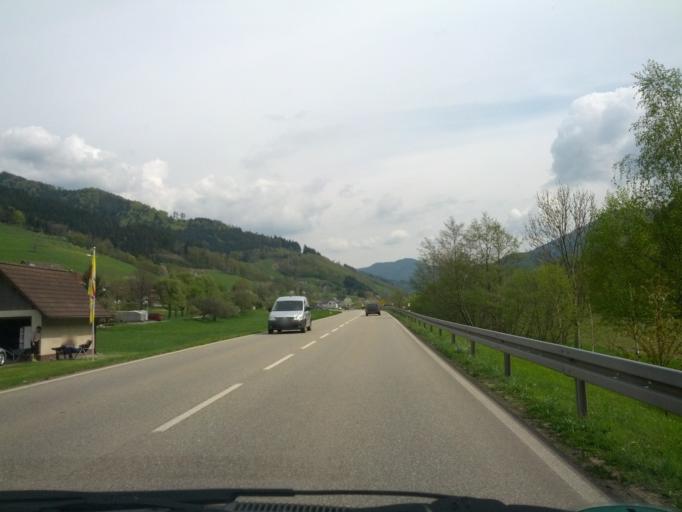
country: DE
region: Baden-Wuerttemberg
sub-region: Freiburg Region
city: Gutach im Breisgau
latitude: 48.1181
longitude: 8.0202
